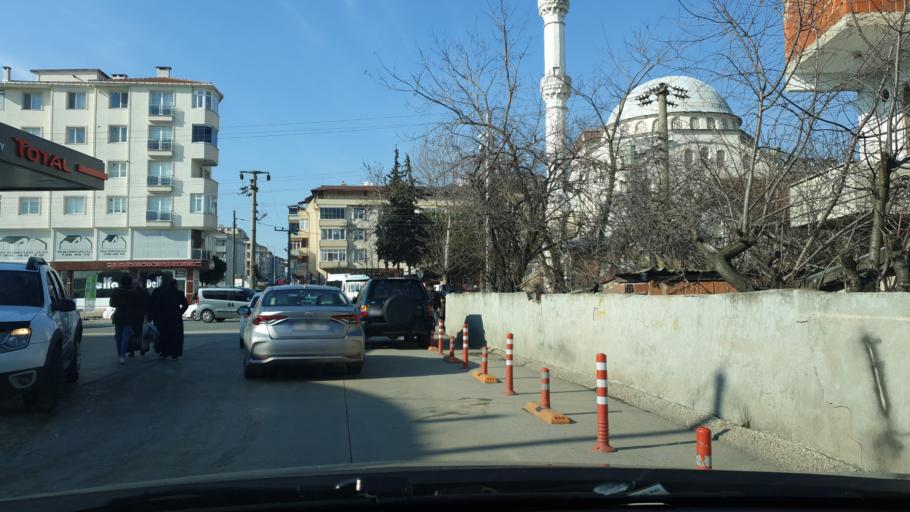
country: TR
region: Tekirdag
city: Cerkezkoey
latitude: 41.2814
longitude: 27.9970
